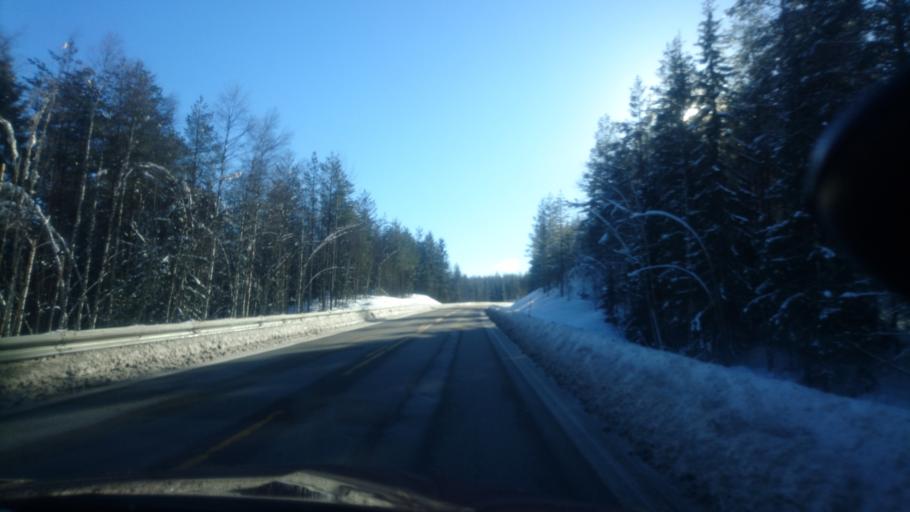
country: NO
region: Hedmark
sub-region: Trysil
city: Innbygda
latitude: 61.2653
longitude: 12.3072
